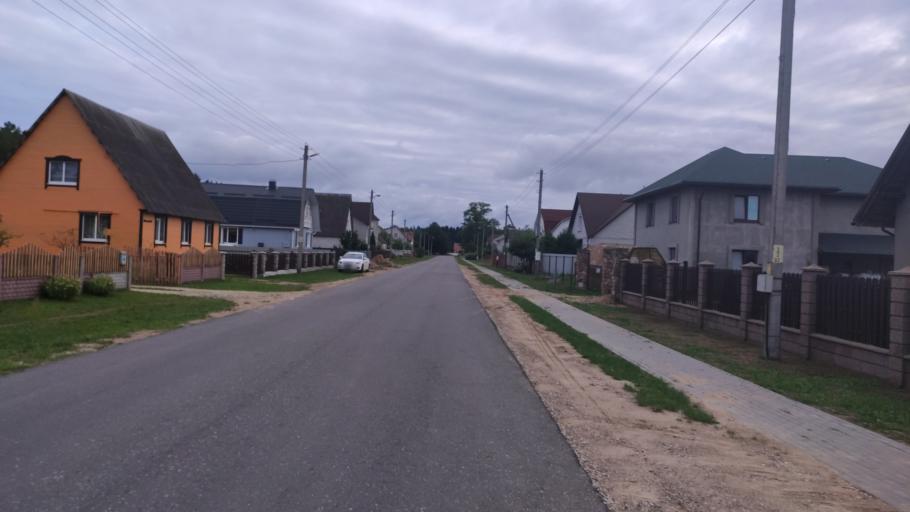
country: BY
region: Minsk
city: Narach
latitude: 54.9270
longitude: 26.6946
